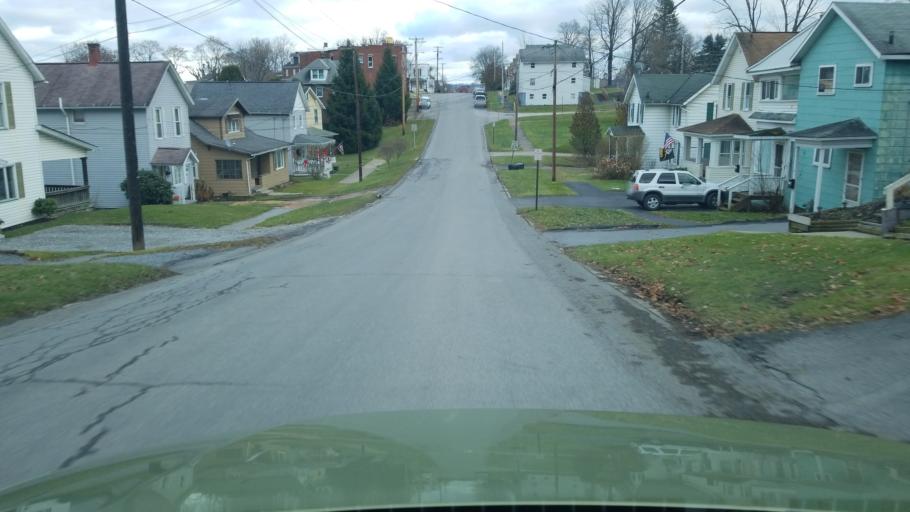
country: US
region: Pennsylvania
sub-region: Clearfield County
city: DuBois
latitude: 41.1232
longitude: -78.7715
